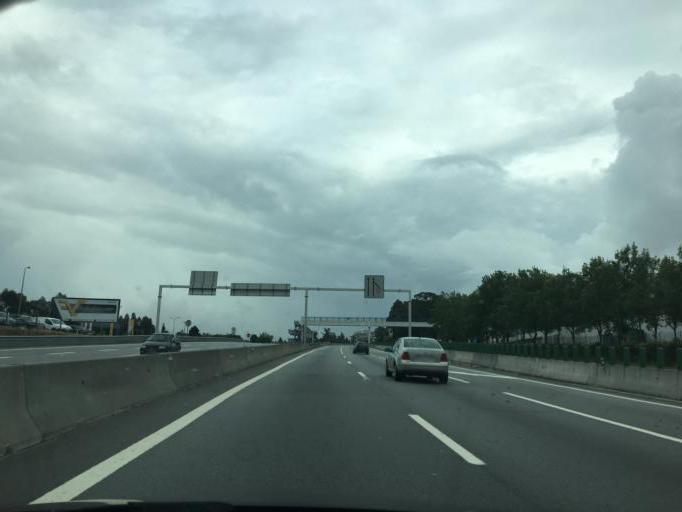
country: PT
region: Porto
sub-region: Maia
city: Leca do Bailio
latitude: 41.1997
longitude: -8.6274
